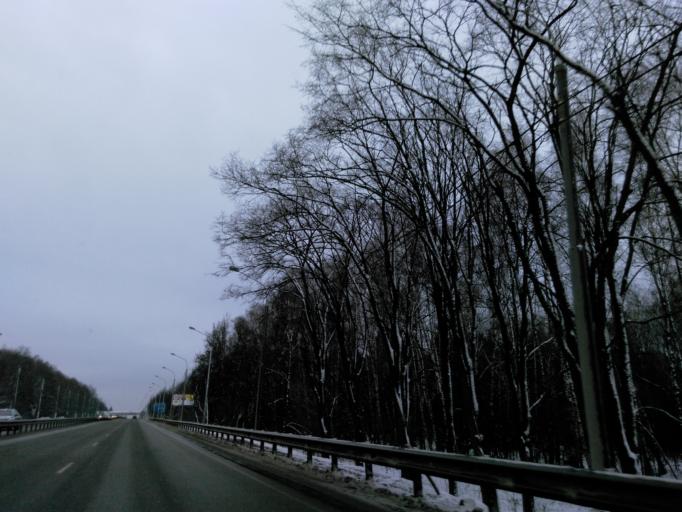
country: RU
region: Moskovskaya
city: Mendeleyevo
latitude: 56.0129
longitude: 37.2111
